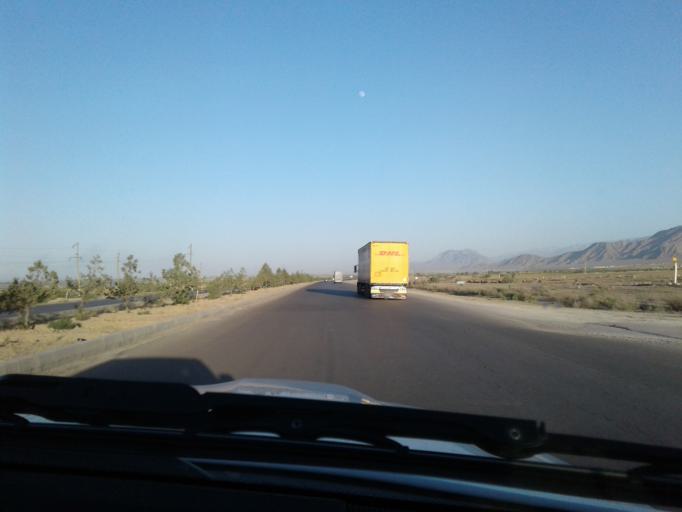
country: TM
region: Ahal
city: Baharly
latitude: 38.2290
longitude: 57.7885
